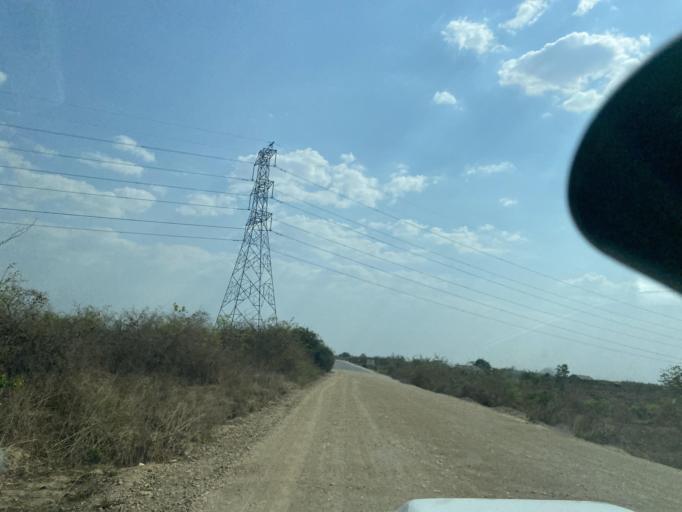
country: ZM
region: Lusaka
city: Lusaka
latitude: -15.3683
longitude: 28.0831
